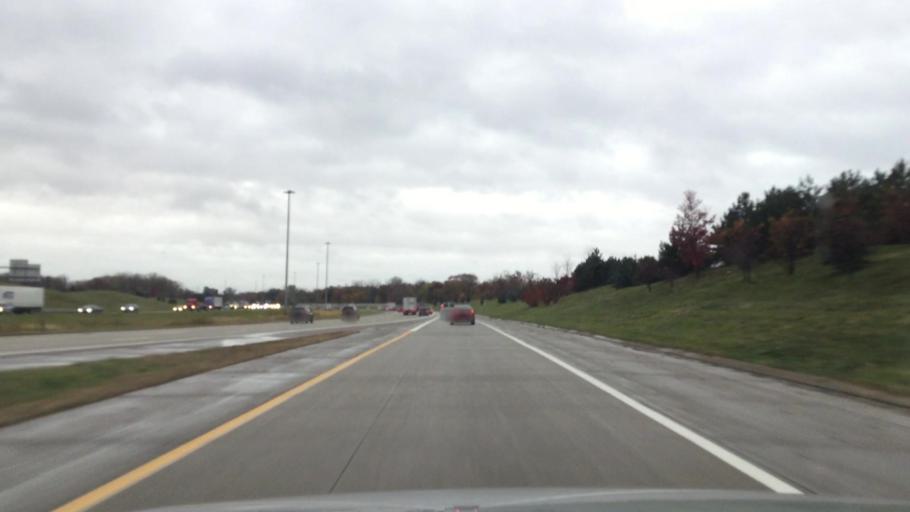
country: US
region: Michigan
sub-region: Wayne County
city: Taylor
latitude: 42.2650
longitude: -83.2765
